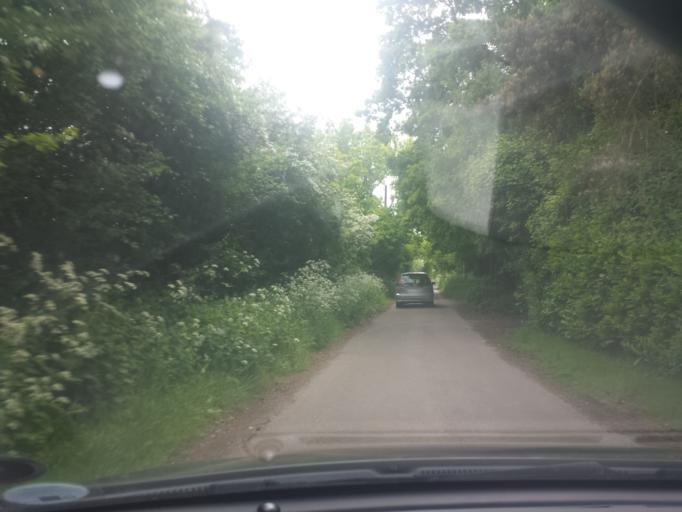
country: GB
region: England
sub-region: Essex
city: Little Clacton
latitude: 51.8672
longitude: 1.1384
